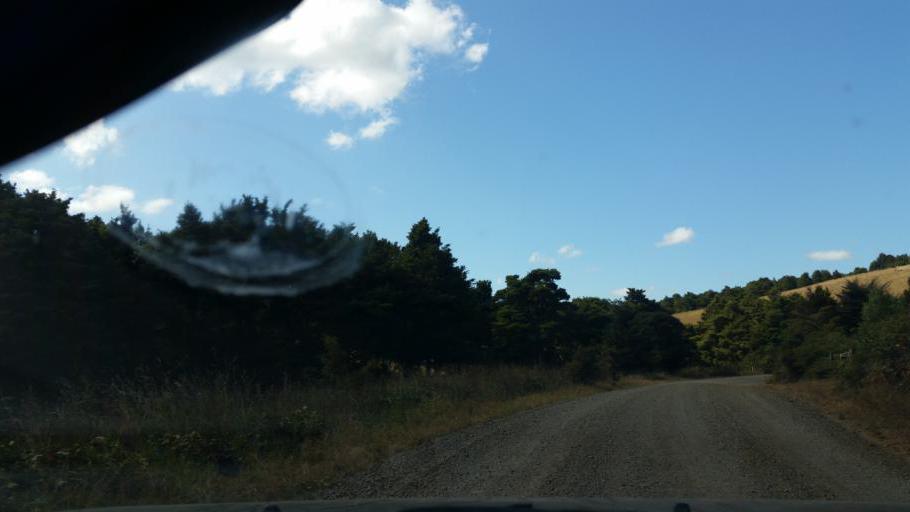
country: NZ
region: Northland
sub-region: Kaipara District
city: Dargaville
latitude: -35.7086
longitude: 173.6085
